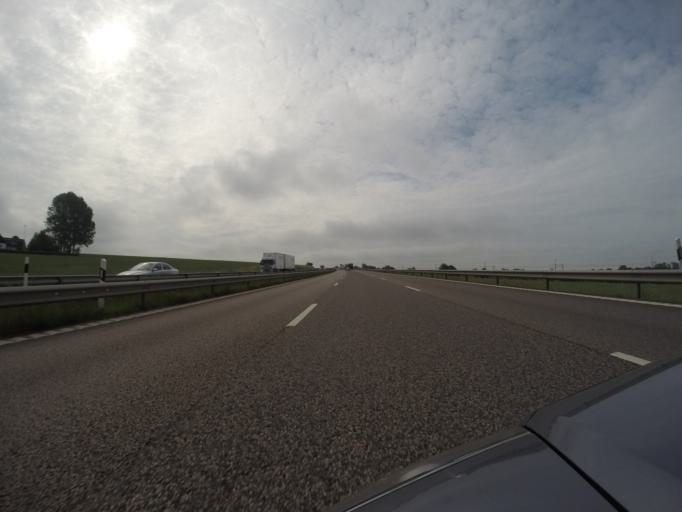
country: SE
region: Skane
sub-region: Helsingborg
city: Glumslov
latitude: 55.9537
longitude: 12.8051
